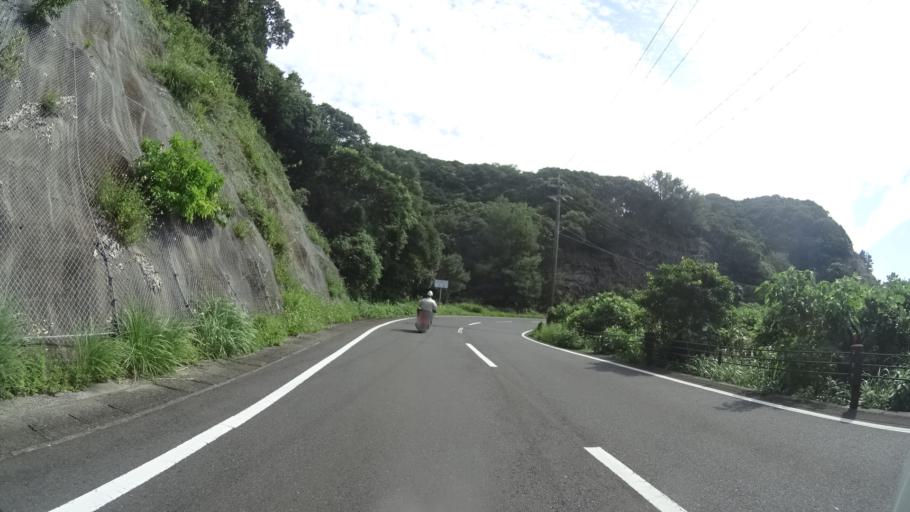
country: JP
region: Kagoshima
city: Nishinoomote
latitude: 30.4294
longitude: 130.4502
